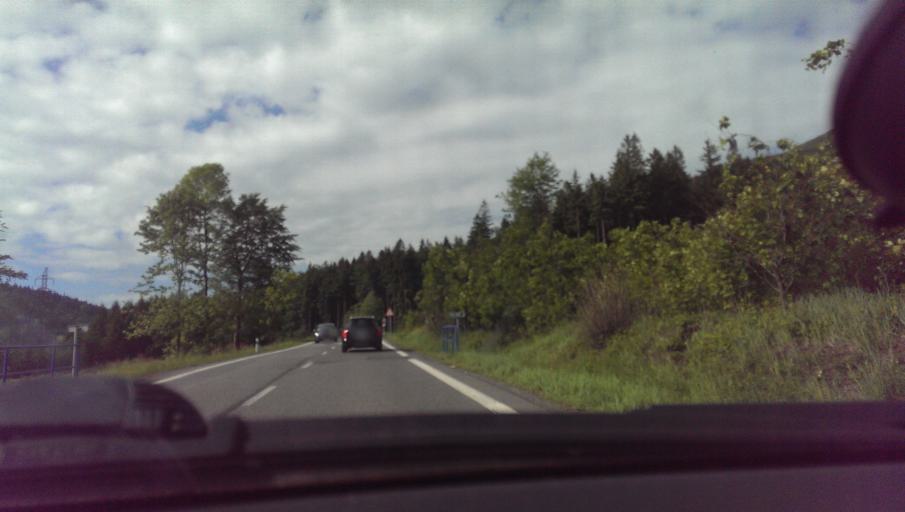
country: CZ
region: Moravskoslezsky
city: Frenstat pod Radhostem
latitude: 49.5080
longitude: 18.1927
